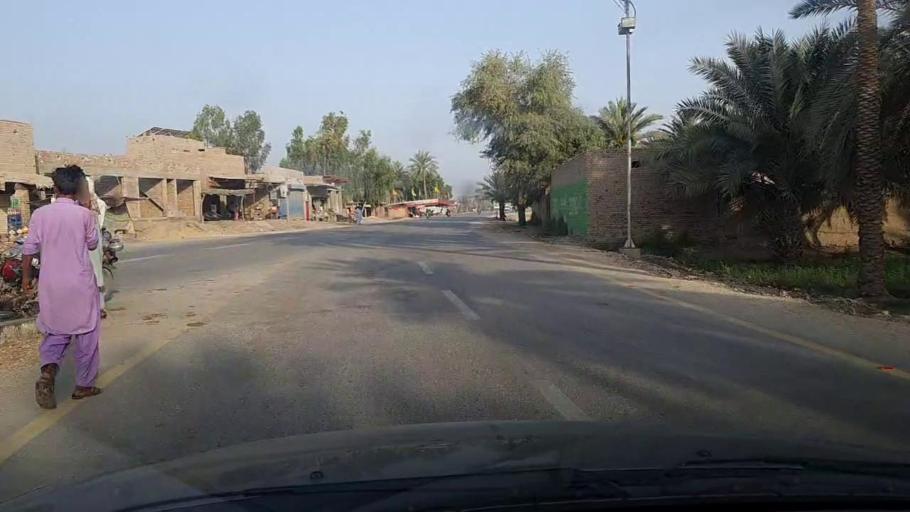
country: PK
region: Sindh
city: Khairpur
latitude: 27.5385
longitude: 68.7119
